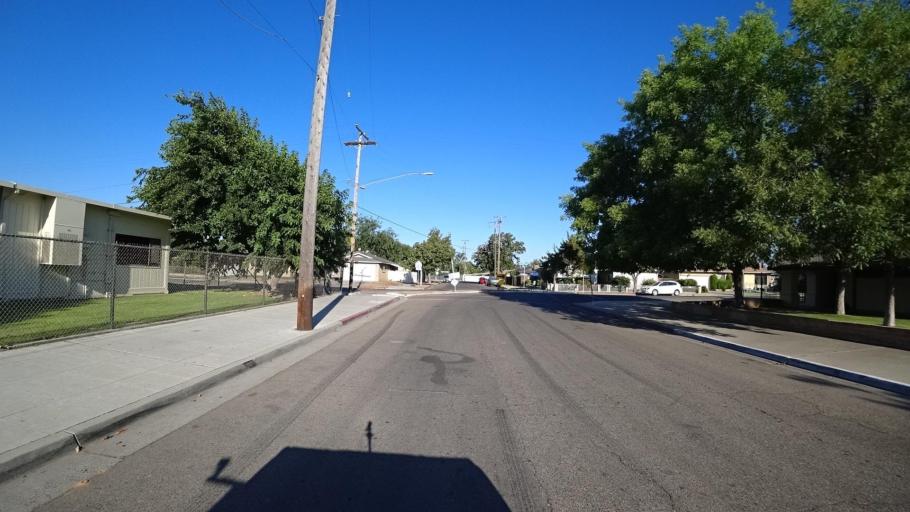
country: US
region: California
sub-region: Fresno County
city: Fresno
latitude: 36.7757
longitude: -119.8308
